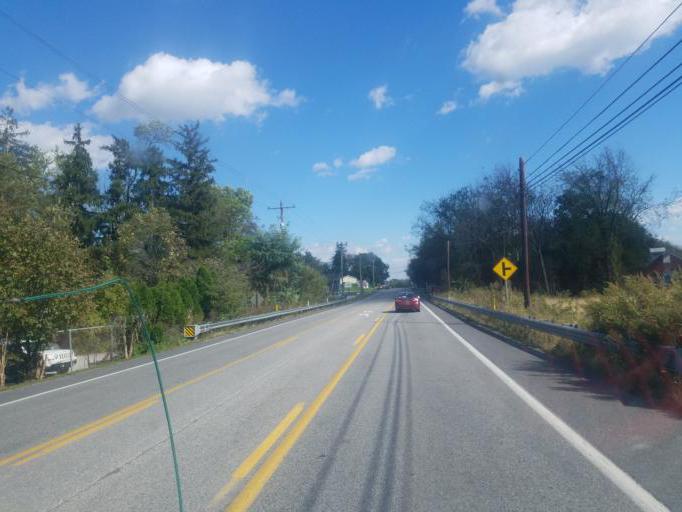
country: US
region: Pennsylvania
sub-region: Adams County
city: Bonneauville
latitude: 39.8583
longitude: -77.1408
